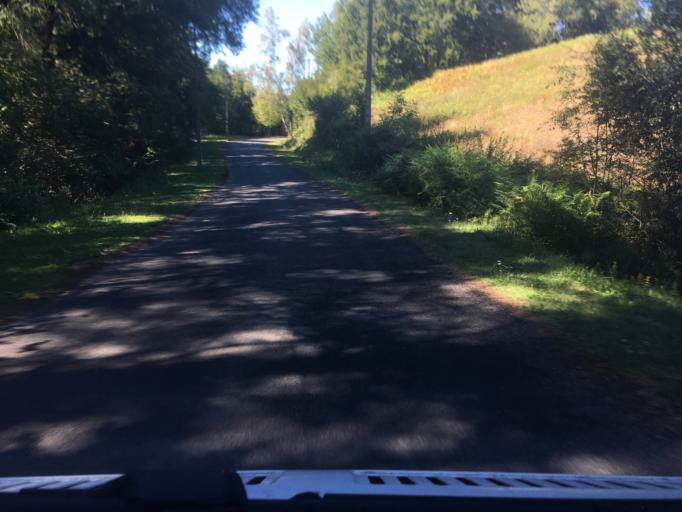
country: FR
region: Auvergne
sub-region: Departement du Cantal
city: Lanobre
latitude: 45.4292
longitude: 2.5045
